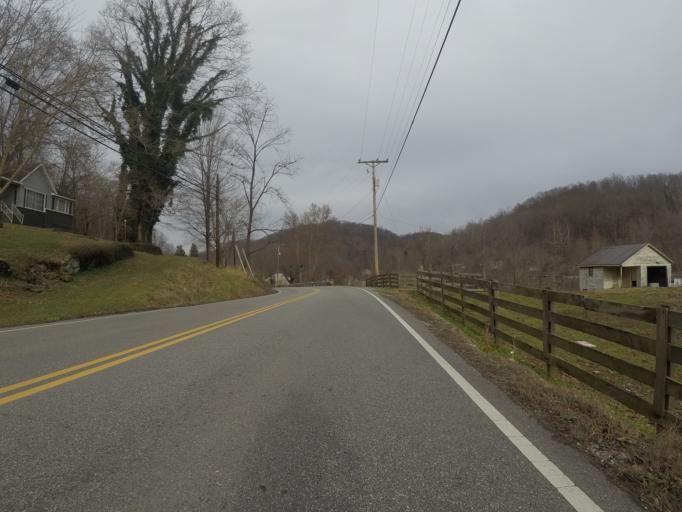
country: US
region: West Virginia
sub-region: Cabell County
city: Huntington
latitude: 38.4380
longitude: -82.4652
